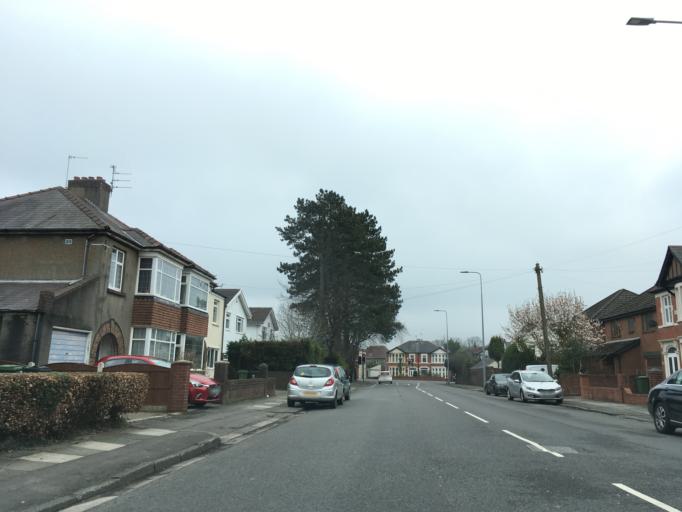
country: GB
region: Wales
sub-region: Cardiff
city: Cardiff
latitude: 51.5176
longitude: -3.1868
